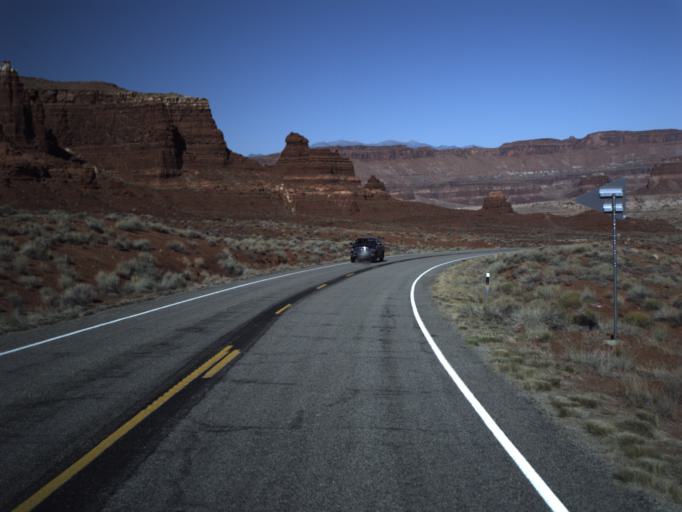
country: US
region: Utah
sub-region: San Juan County
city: Blanding
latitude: 37.8727
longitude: -110.3460
